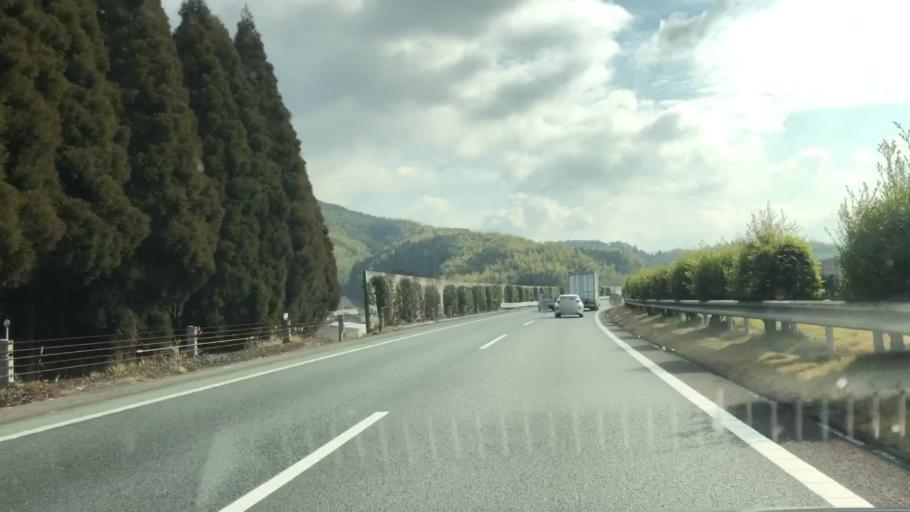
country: JP
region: Fukuoka
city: Setakamachi-takayanagi
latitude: 33.0866
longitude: 130.5408
